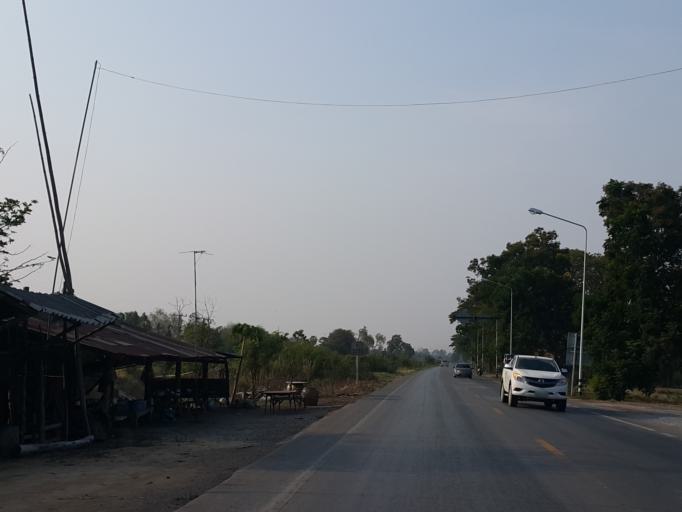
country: TH
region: Chai Nat
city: Sankhaburi
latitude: 15.0222
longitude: 100.1447
